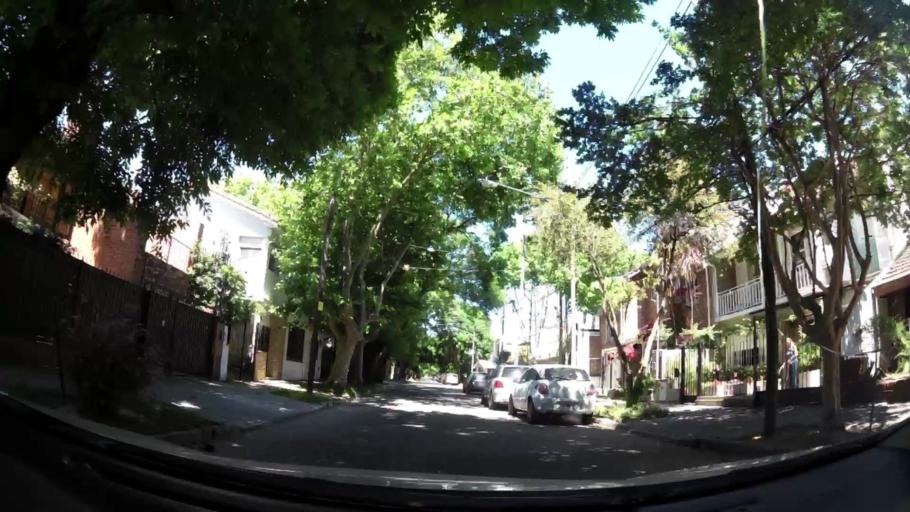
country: AR
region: Buenos Aires
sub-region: Partido de Vicente Lopez
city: Olivos
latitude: -34.5006
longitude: -58.4881
